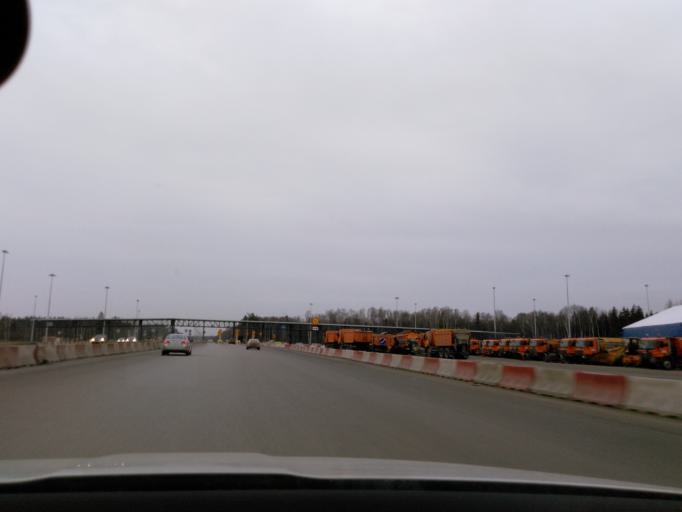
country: RU
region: Moscow
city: Khimki
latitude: 55.9376
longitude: 37.4500
